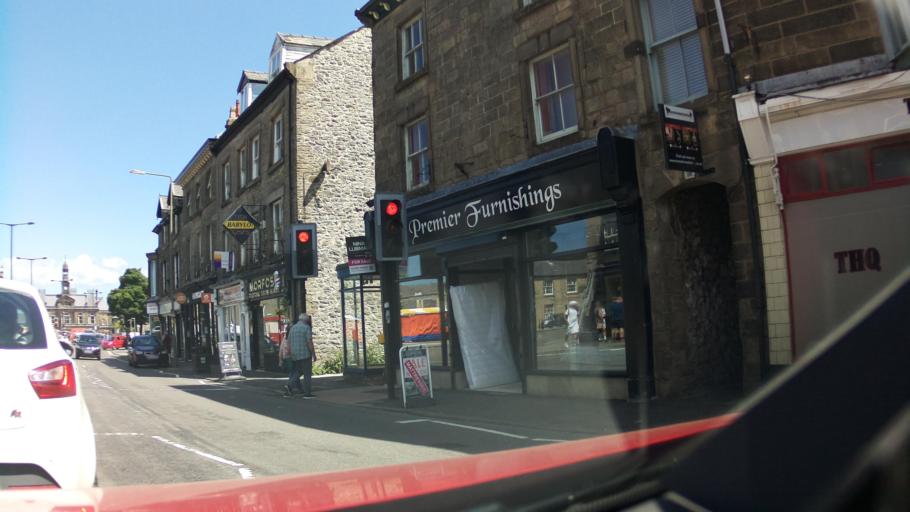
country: GB
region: England
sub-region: Derbyshire
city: Buxton
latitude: 53.2549
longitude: -1.9153
